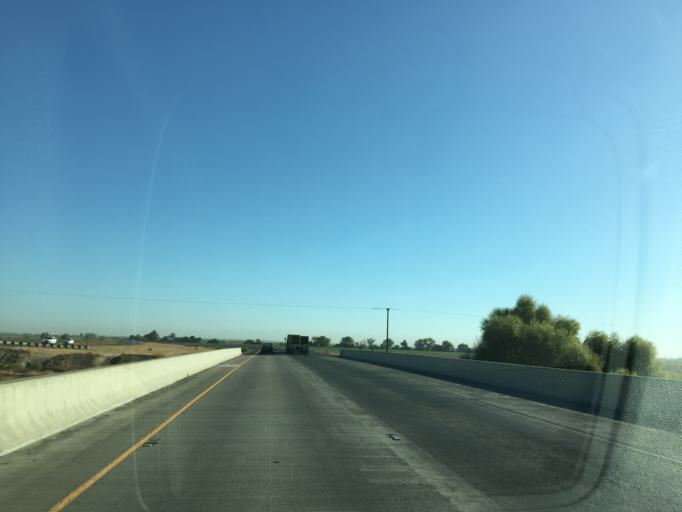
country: US
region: California
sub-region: Merced County
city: Dos Palos
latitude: 37.0555
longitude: -120.5503
